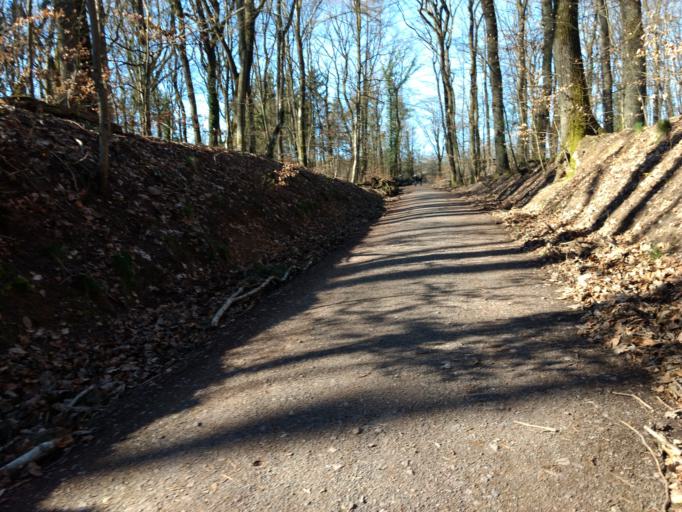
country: DE
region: Saarland
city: Dillingen
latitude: 49.3643
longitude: 6.7309
